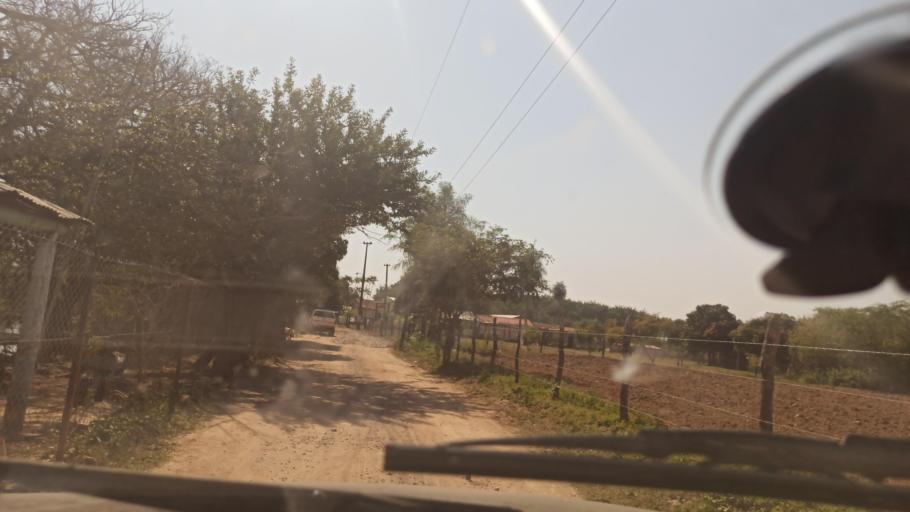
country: AR
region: Formosa
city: Clorinda
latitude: -25.3087
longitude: -57.6975
